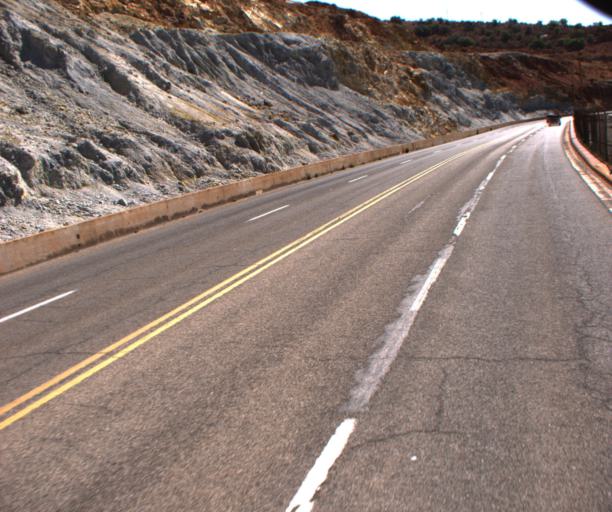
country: US
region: Arizona
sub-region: Cochise County
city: Bisbee
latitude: 31.4361
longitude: -109.8994
